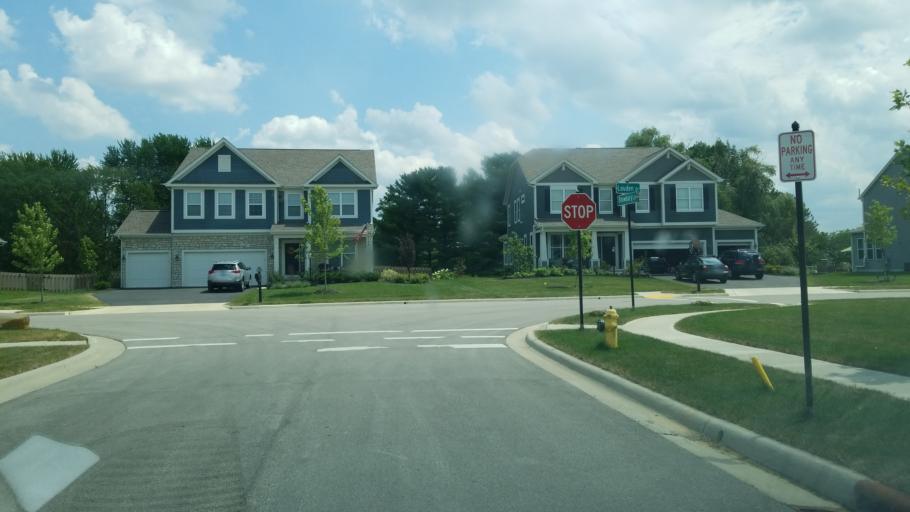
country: US
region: Ohio
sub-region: Delaware County
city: Lewis Center
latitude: 40.2101
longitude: -83.0153
